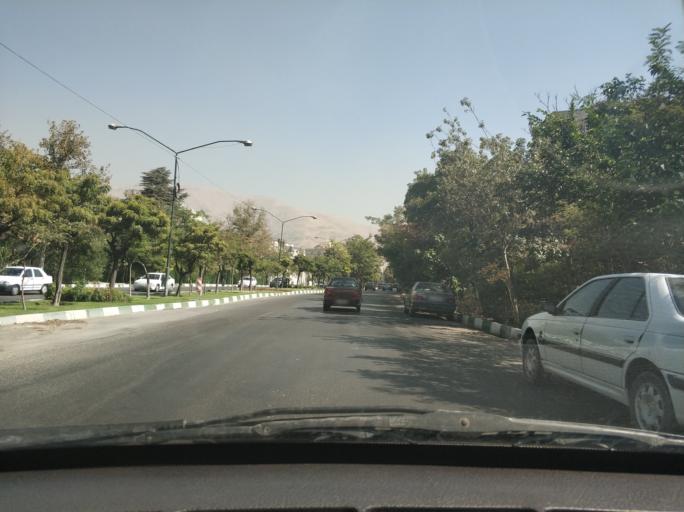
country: IR
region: Tehran
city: Tajrish
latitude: 35.7914
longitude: 51.4742
